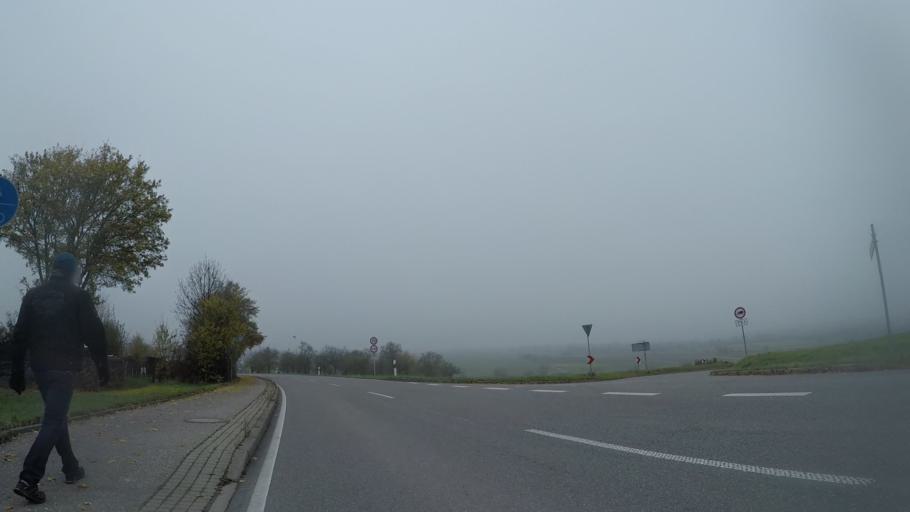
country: DE
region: Baden-Wuerttemberg
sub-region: Tuebingen Region
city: Sickenhausen
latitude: 48.5167
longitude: 9.1899
